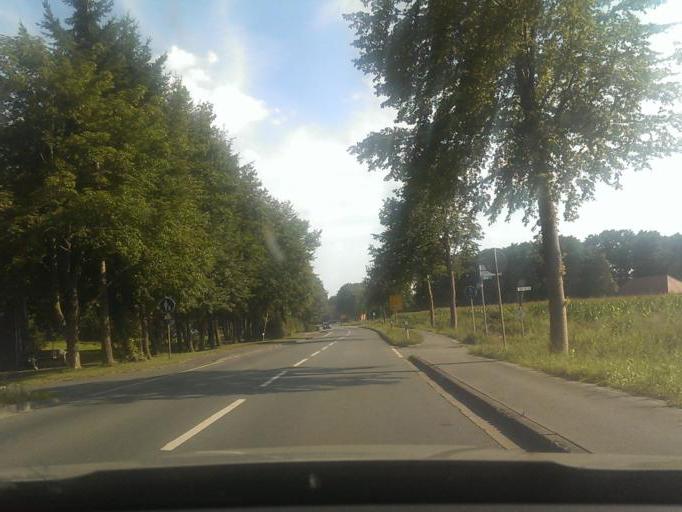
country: DE
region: North Rhine-Westphalia
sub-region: Regierungsbezirk Detmold
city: Delbruck
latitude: 51.7216
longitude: 8.5643
